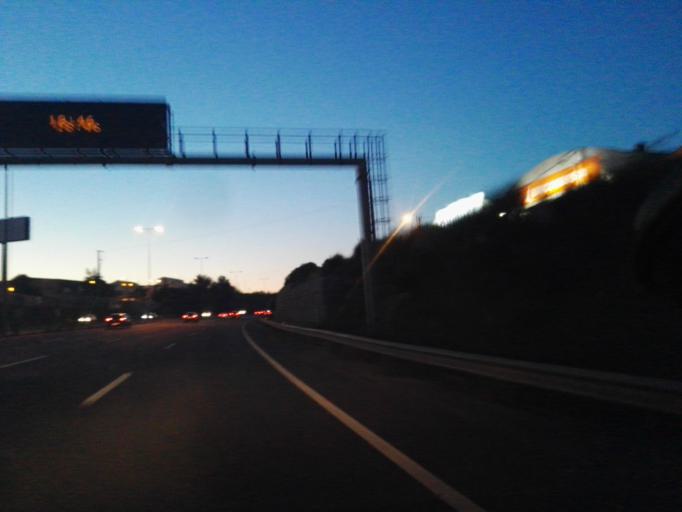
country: PT
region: Lisbon
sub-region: Loures
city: Camarate
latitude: 38.7963
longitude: -9.1210
